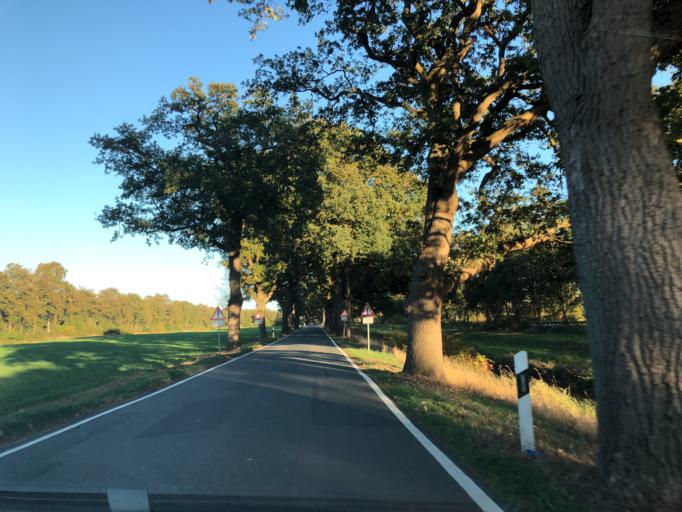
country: DE
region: Lower Saxony
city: Friesoythe
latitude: 53.0246
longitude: 7.8206
